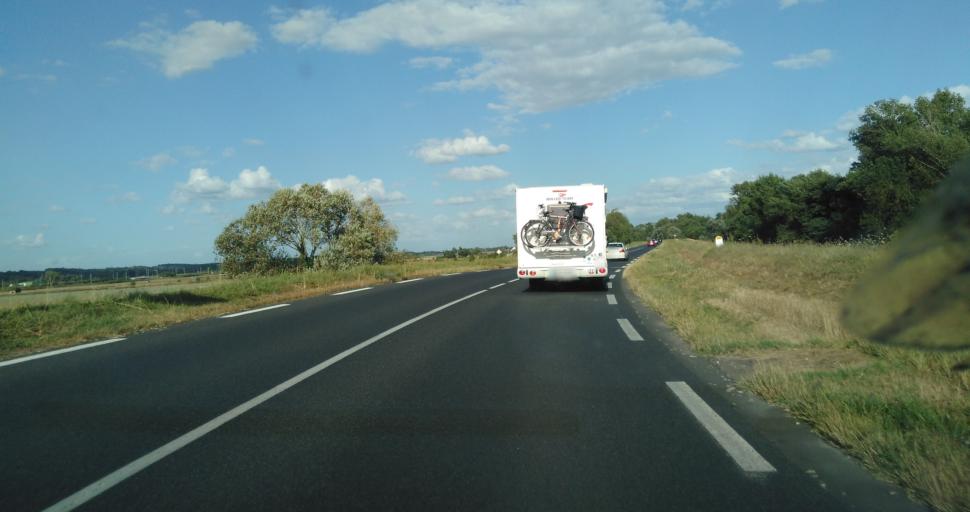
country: FR
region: Centre
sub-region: Departement d'Indre-et-Loire
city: Vernou-sur-Brenne
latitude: 47.4012
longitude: 0.8600
